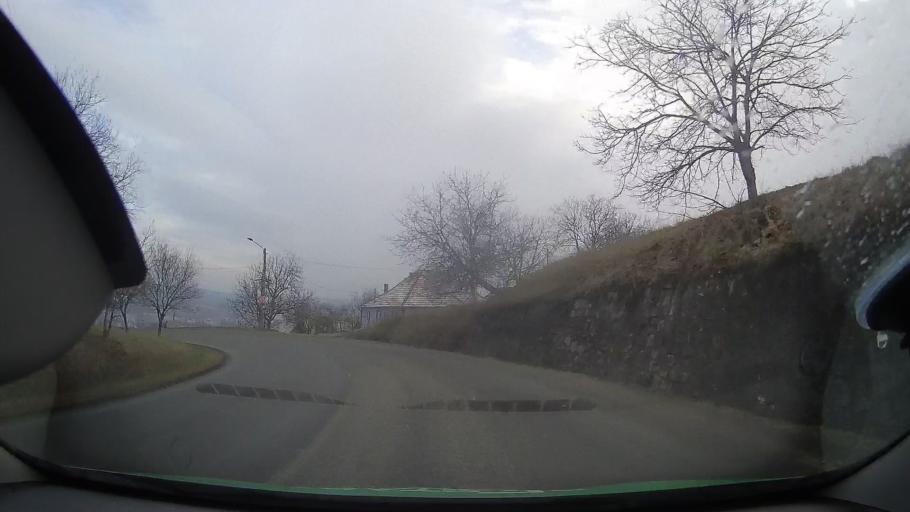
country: RO
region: Mures
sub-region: Municipiul Tarnaveni
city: Tarnaveni
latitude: 46.3360
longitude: 24.2822
